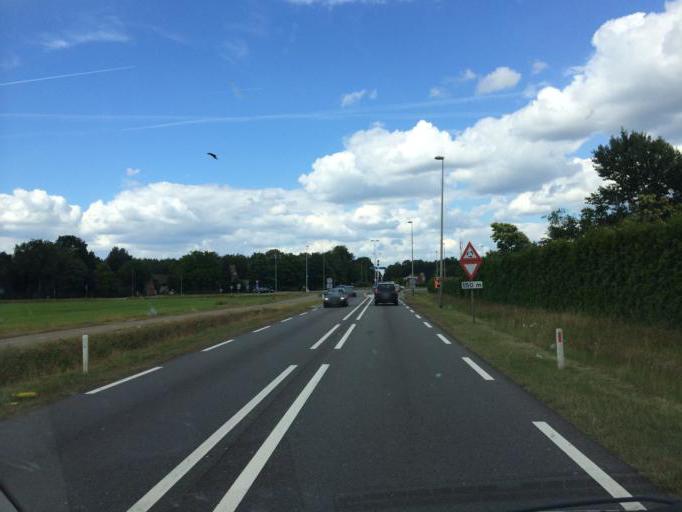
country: NL
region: North Brabant
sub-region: Gemeente Valkenswaard
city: Valkenswaard
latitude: 51.3059
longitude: 5.4218
